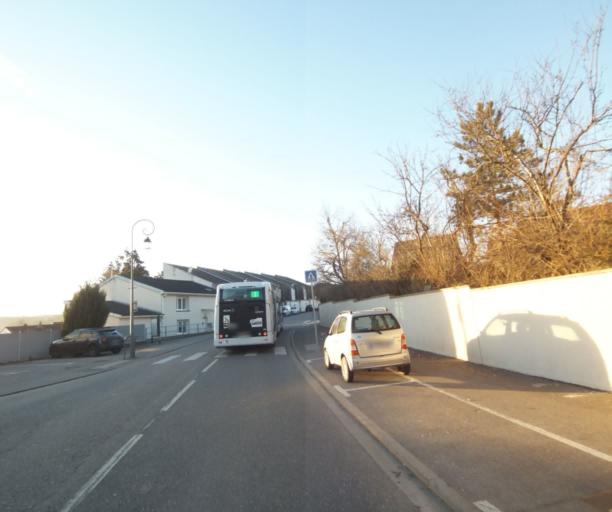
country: FR
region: Lorraine
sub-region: Departement de Meurthe-et-Moselle
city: Seichamps
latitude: 48.7170
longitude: 6.2652
